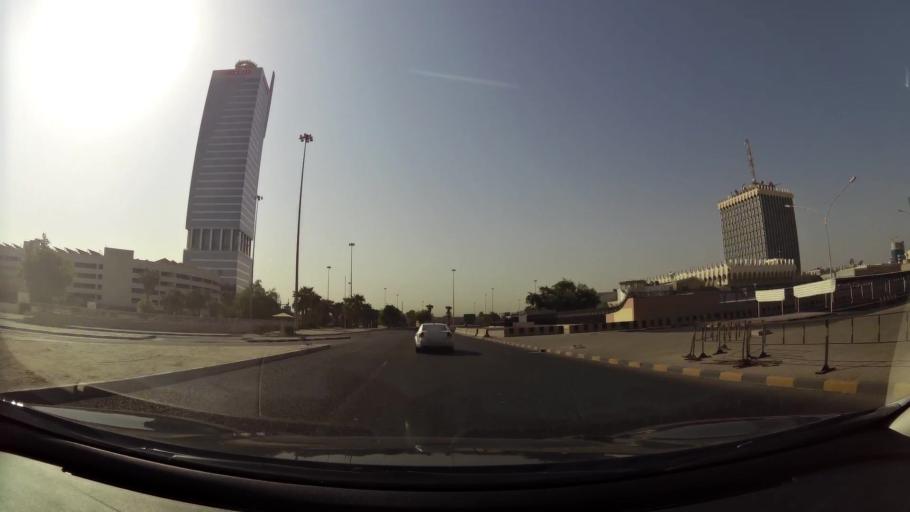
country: KW
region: Al Asimah
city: Kuwait City
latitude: 29.3641
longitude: 47.9742
